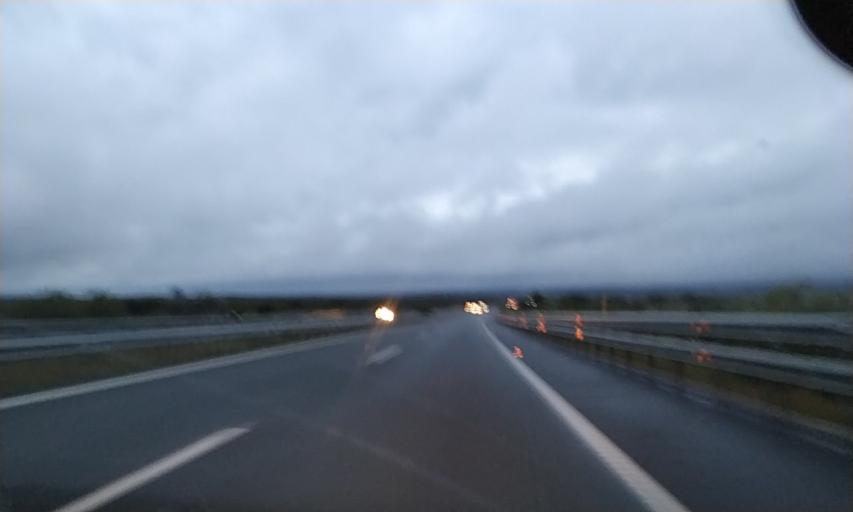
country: ES
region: Extremadura
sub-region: Provincia de Caceres
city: Alcuescar
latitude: 39.1815
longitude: -6.2744
